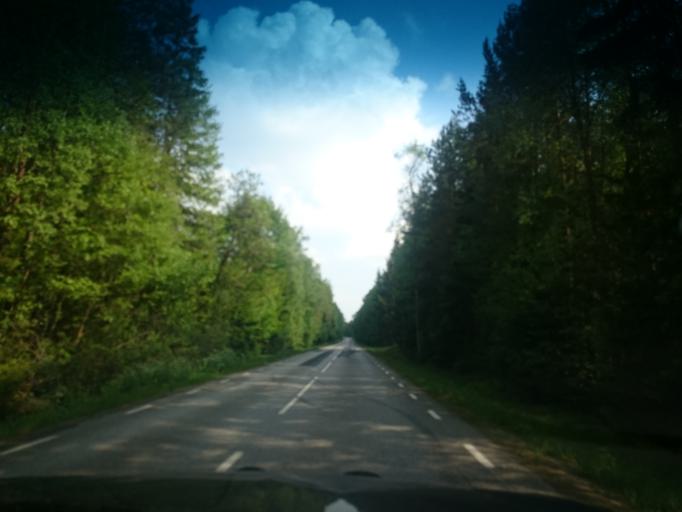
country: SE
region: Joenkoeping
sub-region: Vetlanda Kommun
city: Vetlanda
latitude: 57.3262
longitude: 15.0857
